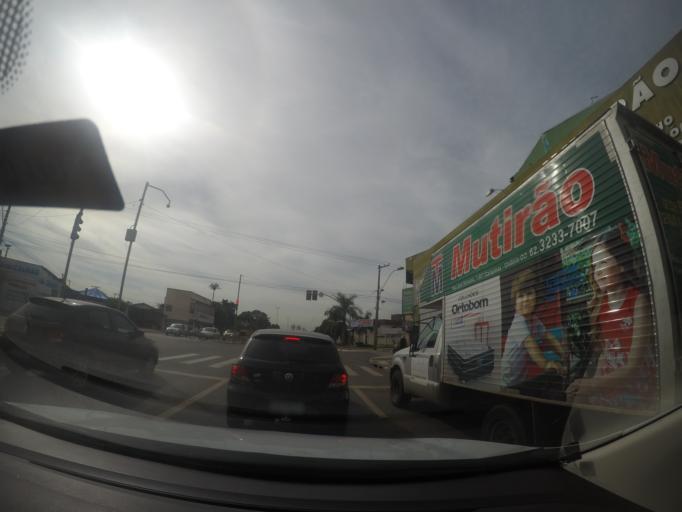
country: BR
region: Goias
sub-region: Goiania
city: Goiania
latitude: -16.6604
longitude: -49.2923
